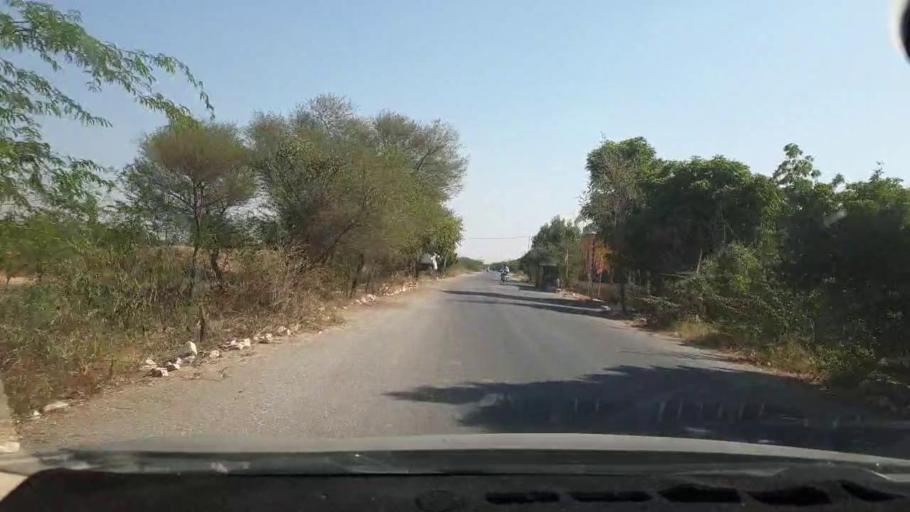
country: PK
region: Sindh
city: Malir Cantonment
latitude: 25.1414
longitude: 67.1998
